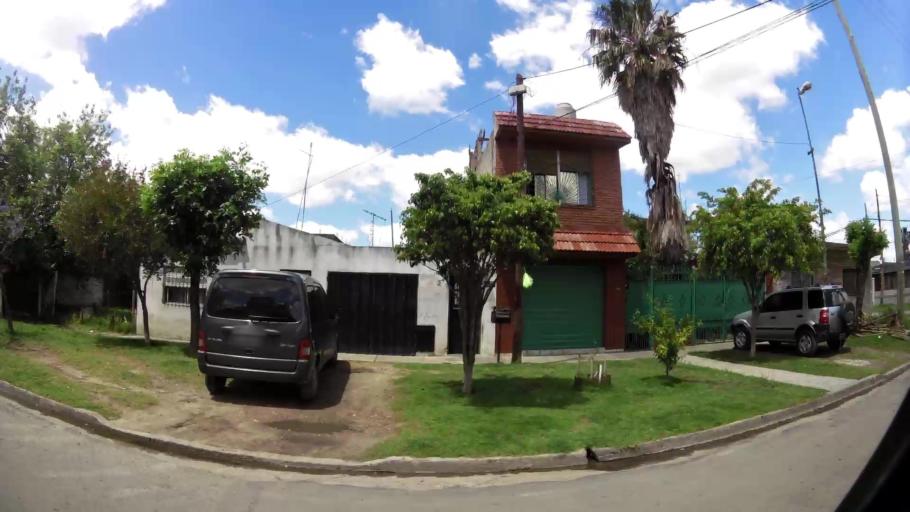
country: AR
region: Buenos Aires
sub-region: Partido de Lanus
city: Lanus
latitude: -34.6955
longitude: -58.4347
